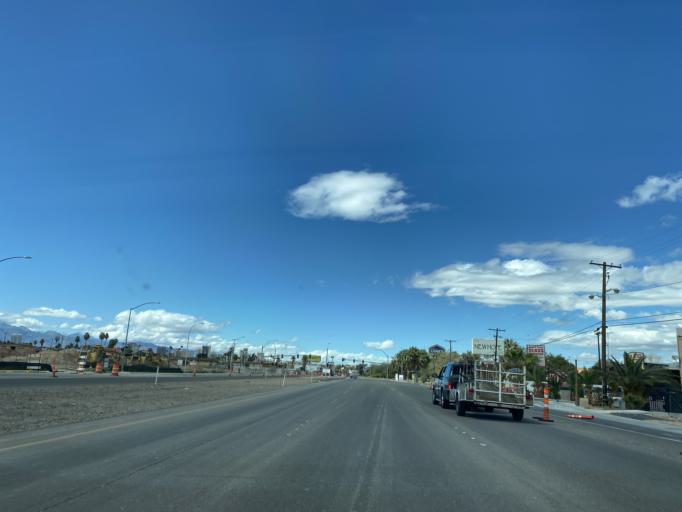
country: US
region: Nevada
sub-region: Clark County
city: Winchester
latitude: 36.1542
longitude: -115.1108
